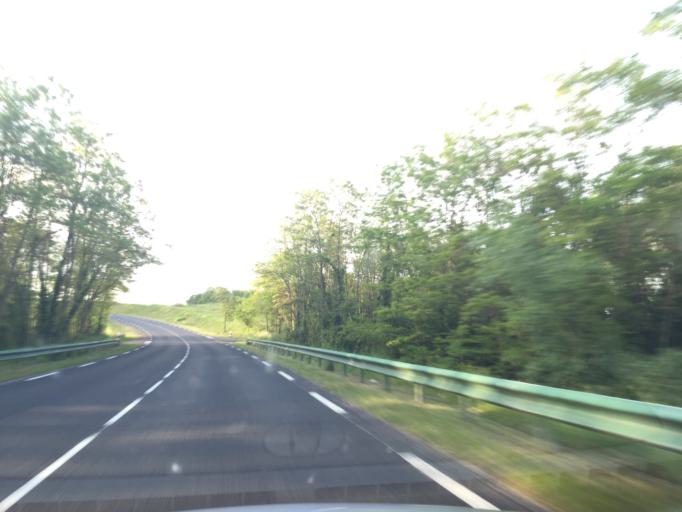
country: FR
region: Auvergne
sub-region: Departement du Puy-de-Dome
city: Chatel-Guyon
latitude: 45.9224
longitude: 3.0851
